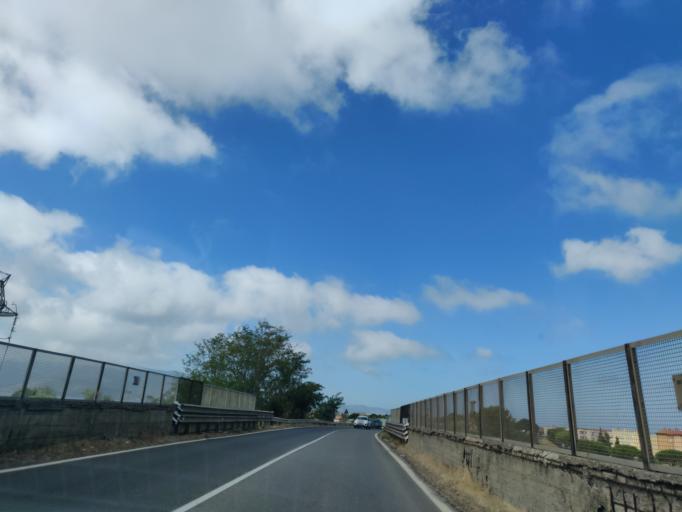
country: IT
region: Tuscany
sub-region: Provincia di Grosseto
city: Orbetello Scalo
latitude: 42.4463
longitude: 11.2546
